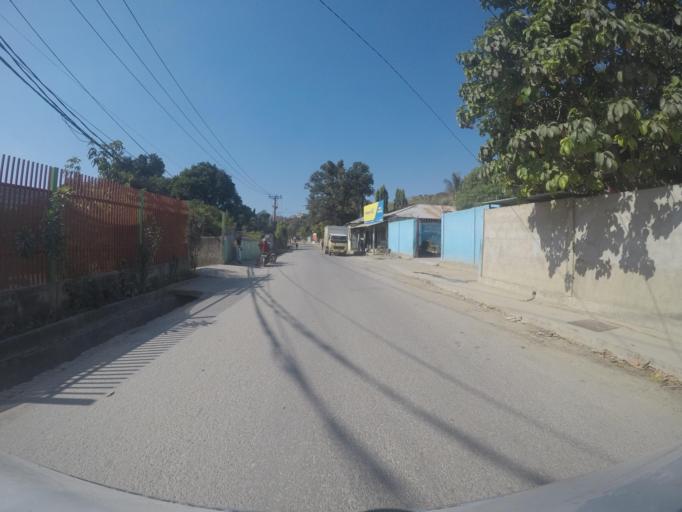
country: TL
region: Dili
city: Dili
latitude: -8.5740
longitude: 125.5423
